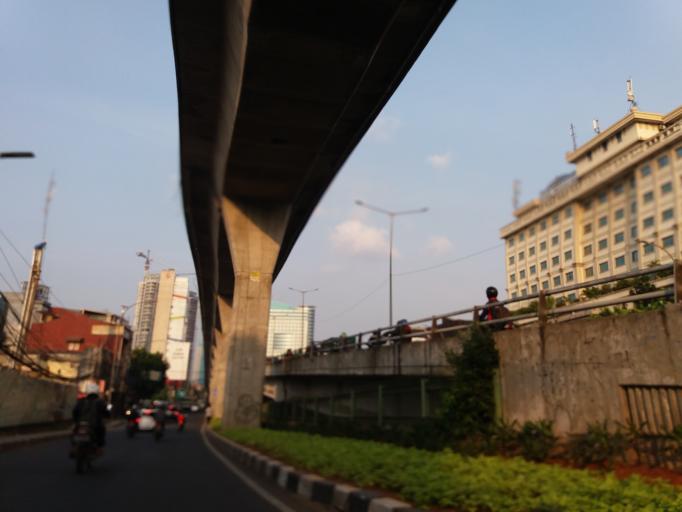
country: ID
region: Jakarta Raya
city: Jakarta
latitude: -6.2400
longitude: 106.8243
